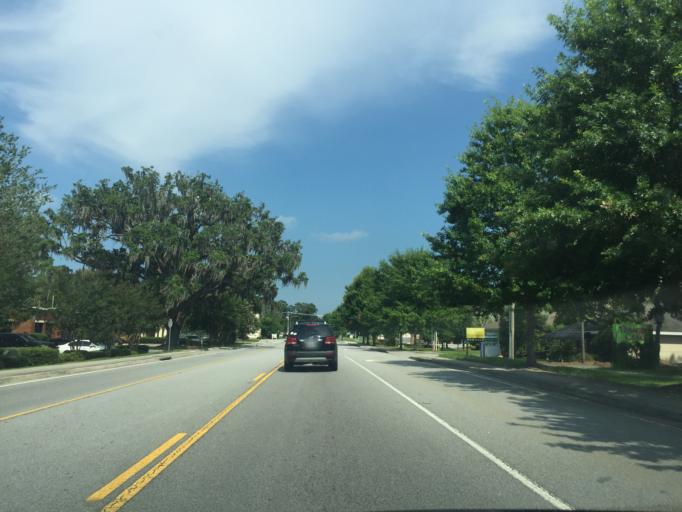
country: US
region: Georgia
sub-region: Chatham County
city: Isle of Hope
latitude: 32.0112
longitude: -81.1040
